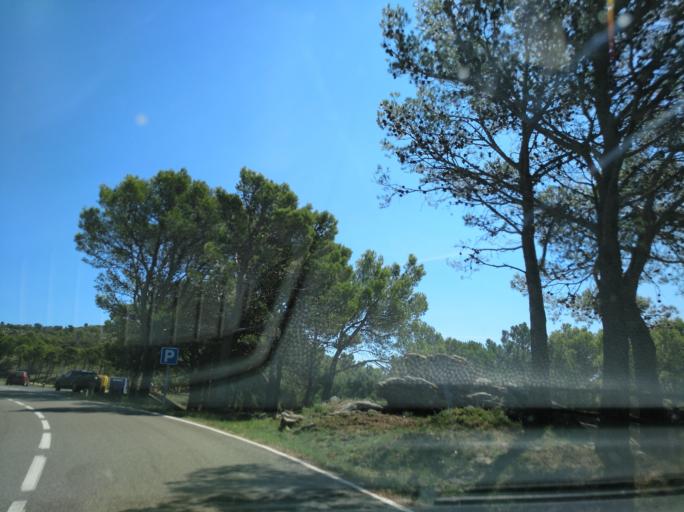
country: ES
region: Catalonia
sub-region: Provincia de Girona
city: Pau
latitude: 42.3260
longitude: 3.1479
